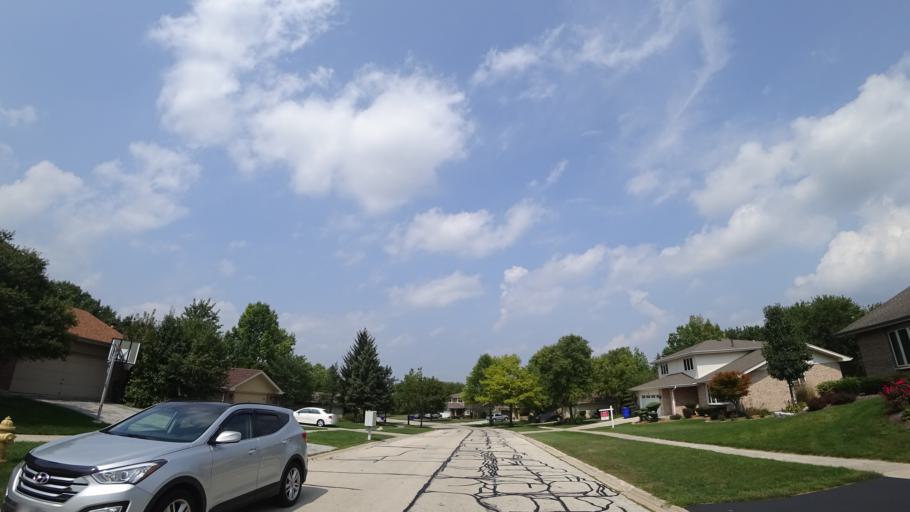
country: US
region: Illinois
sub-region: Will County
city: Goodings Grove
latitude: 41.6254
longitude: -87.8976
